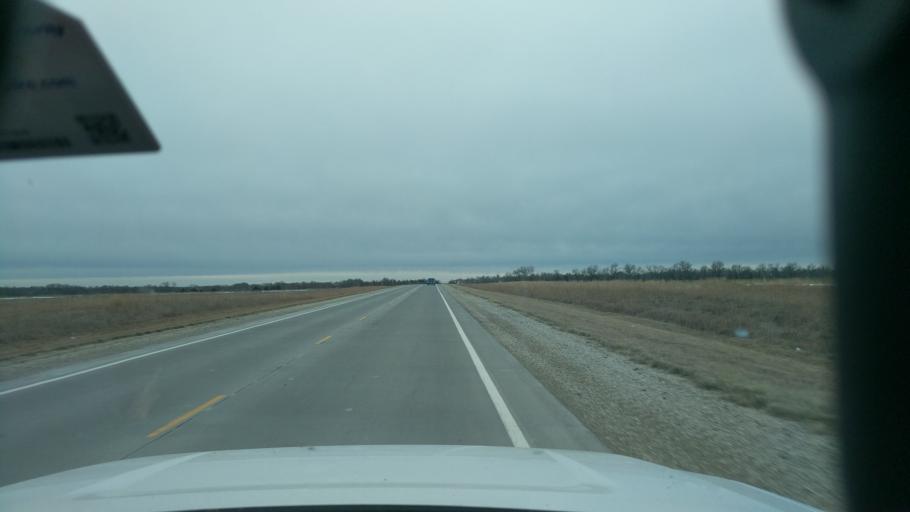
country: US
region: Kansas
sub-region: Marion County
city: Marion
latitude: 38.5040
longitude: -96.9575
